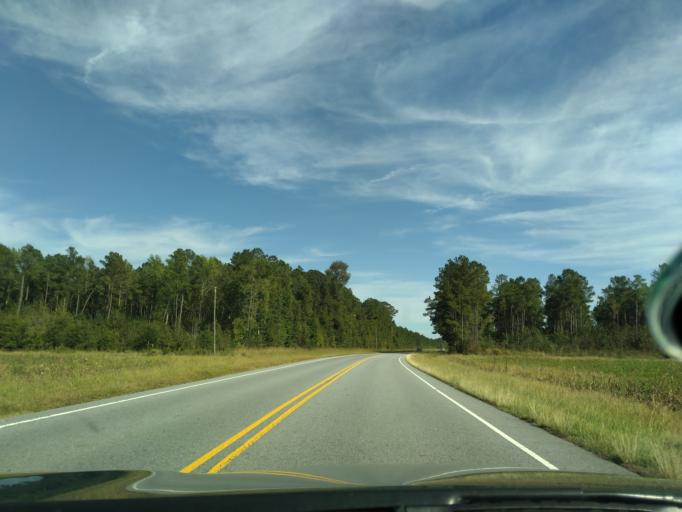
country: US
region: North Carolina
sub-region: Beaufort County
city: River Road
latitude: 35.5258
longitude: -76.8731
